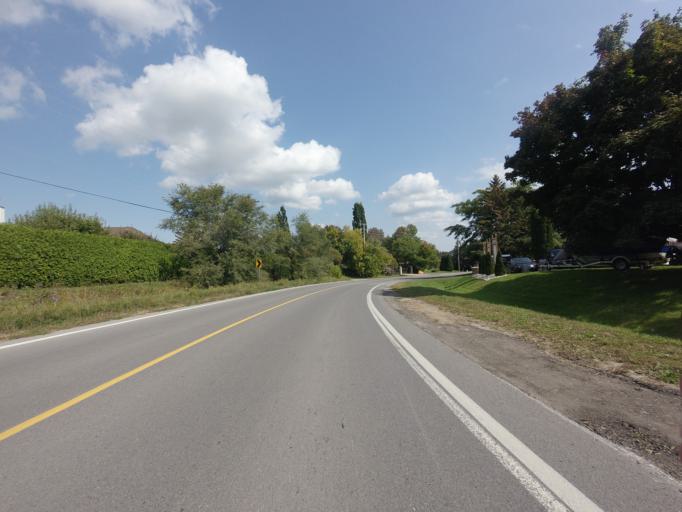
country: CA
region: Ontario
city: Bells Corners
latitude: 45.2399
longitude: -75.6950
